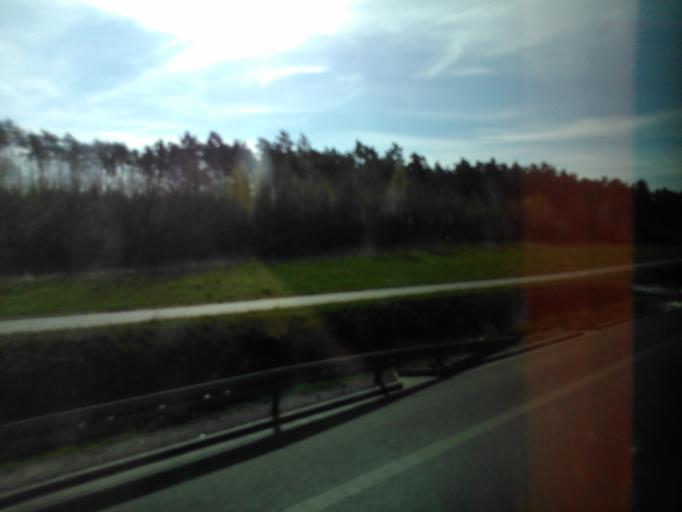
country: PL
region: Kujawsko-Pomorskie
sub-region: Powiat torunski
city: Lubicz Dolny
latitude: 52.9673
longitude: 18.6824
